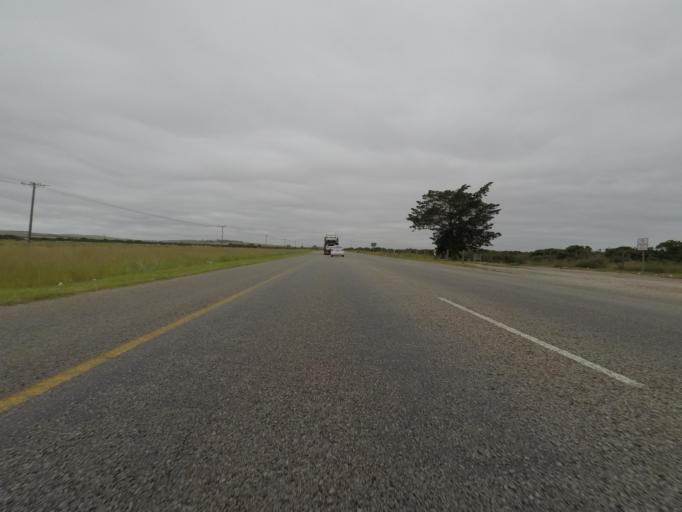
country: ZA
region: Eastern Cape
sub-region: Nelson Mandela Bay Metropolitan Municipality
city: Port Elizabeth
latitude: -33.6552
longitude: 25.8661
